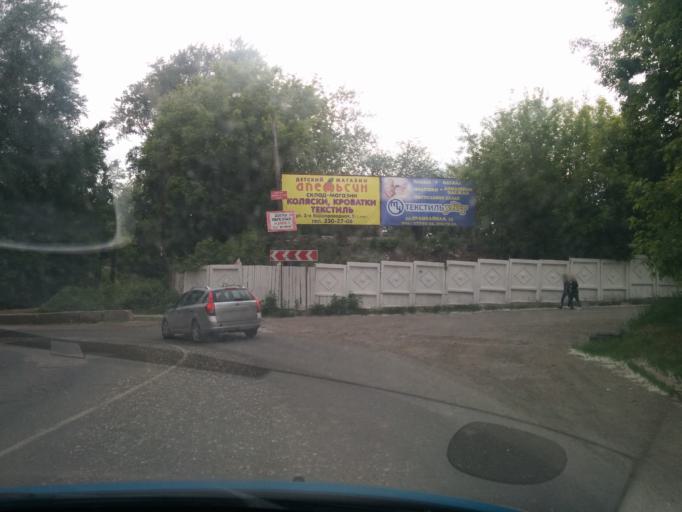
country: RU
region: Perm
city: Perm
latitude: 58.0032
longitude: 56.1824
